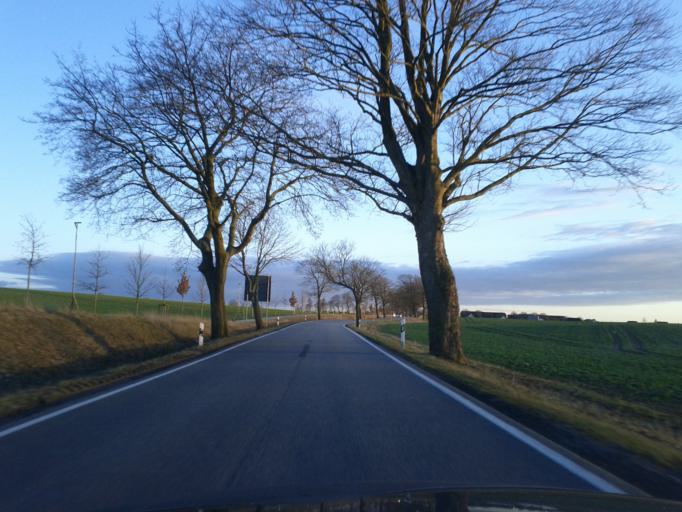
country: DE
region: Mecklenburg-Vorpommern
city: Hornstorf
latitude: 53.9427
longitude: 11.4863
